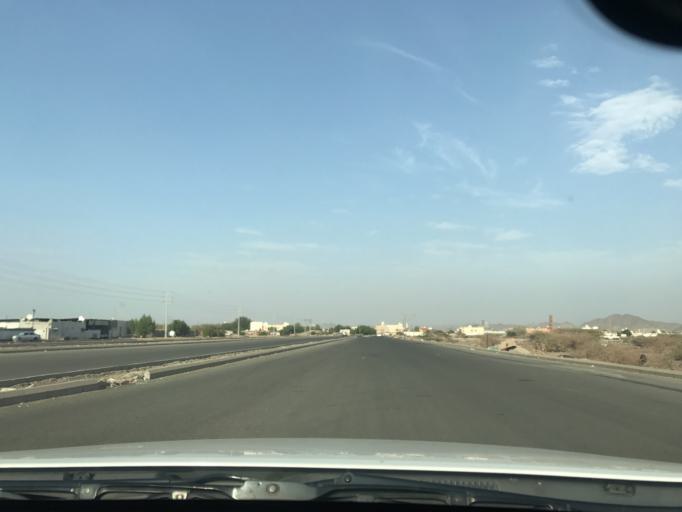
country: SA
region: Makkah
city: Al Jumum
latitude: 21.4539
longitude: 39.5435
